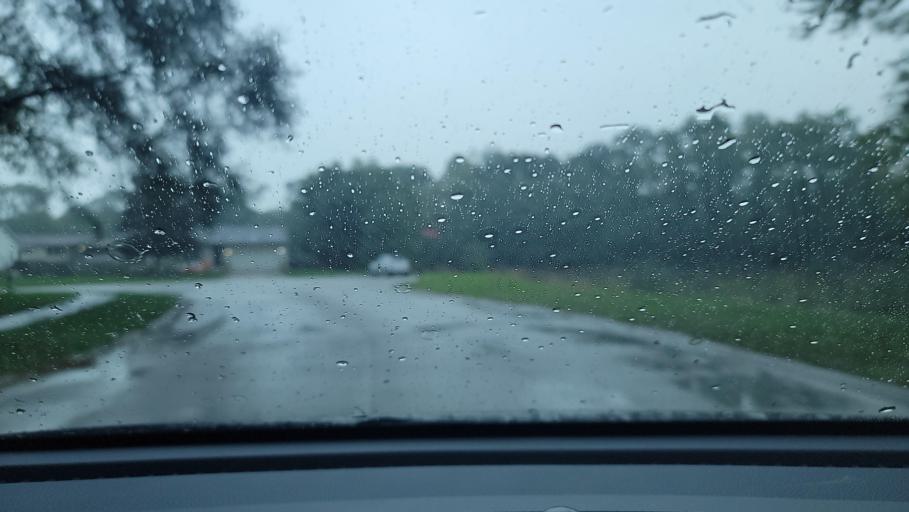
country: US
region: Indiana
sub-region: Porter County
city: Portage
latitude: 41.5900
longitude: -87.1783
